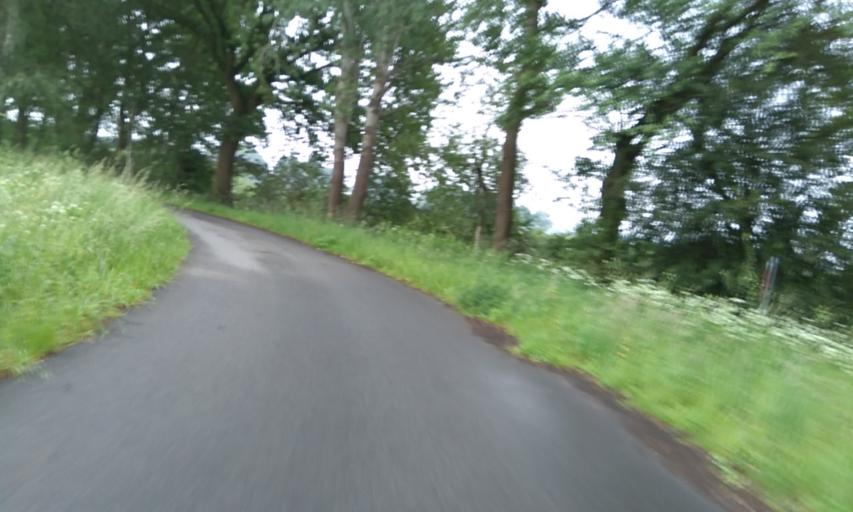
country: DE
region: Lower Saxony
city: Deinste
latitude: 53.5424
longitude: 9.4798
